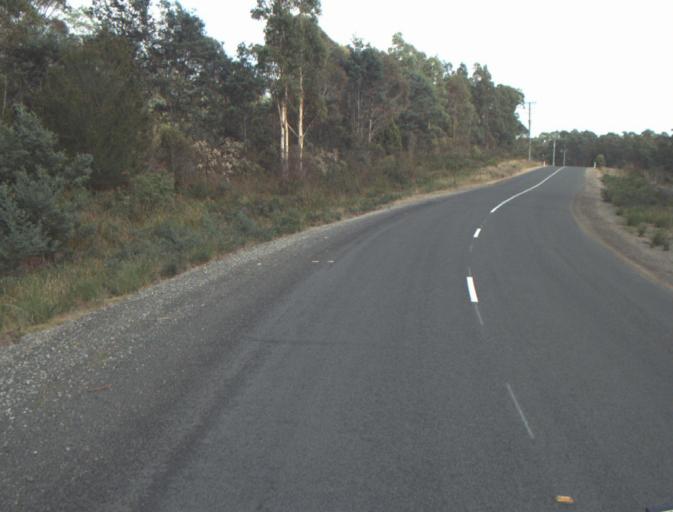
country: AU
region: Tasmania
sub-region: Dorset
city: Bridport
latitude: -41.1365
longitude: 147.2241
